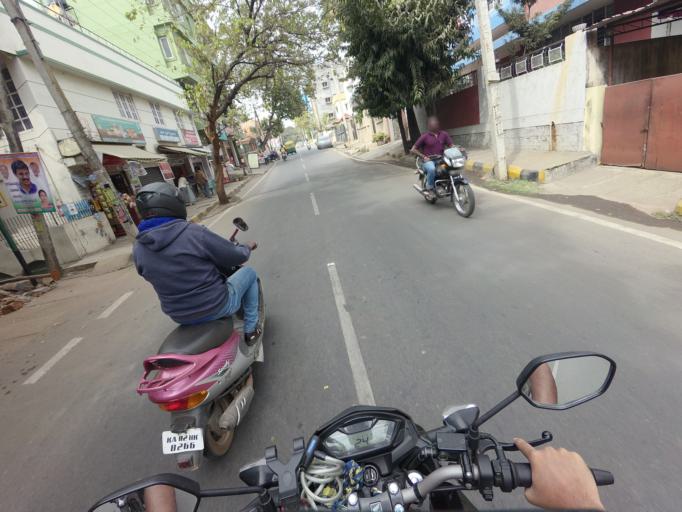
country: IN
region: Karnataka
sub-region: Bangalore Urban
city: Bangalore
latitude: 12.9744
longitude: 77.5338
